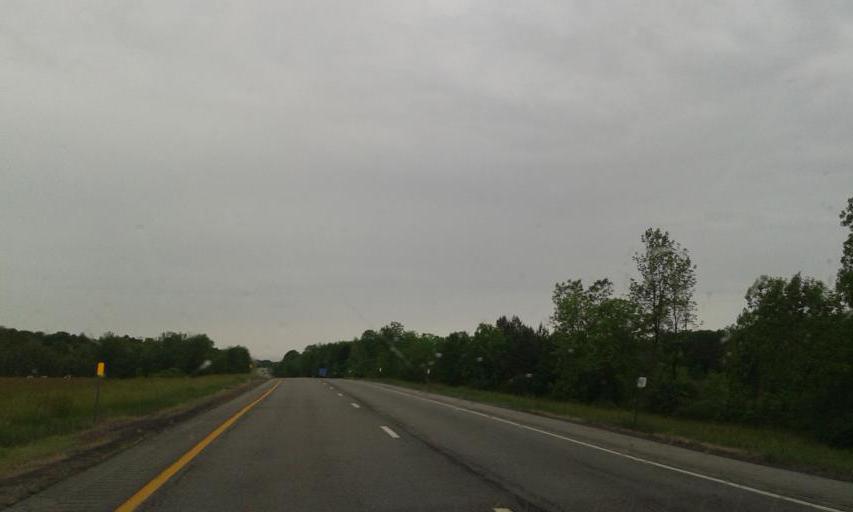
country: US
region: New York
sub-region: Genesee County
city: Bergen
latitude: 43.0302
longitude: -77.9191
